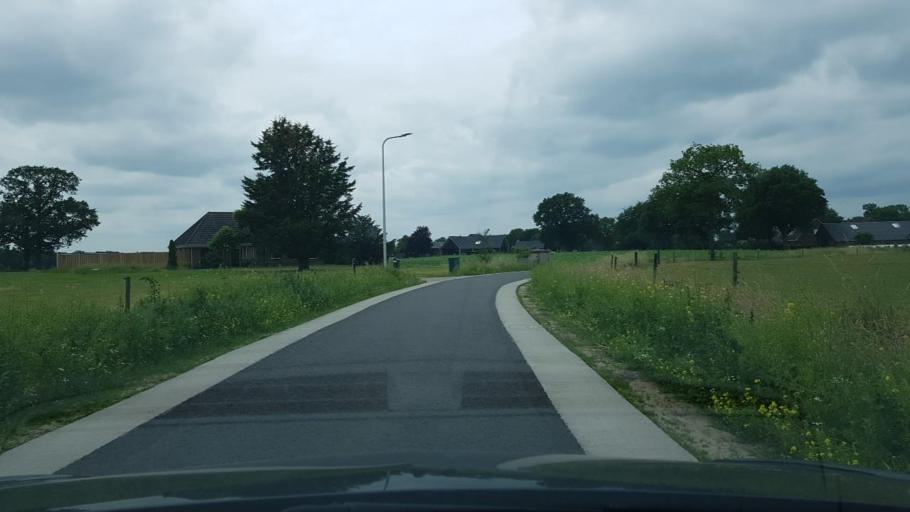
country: NL
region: Overijssel
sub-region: Gemeente Raalte
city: Raalte
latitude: 52.3524
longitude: 6.3803
